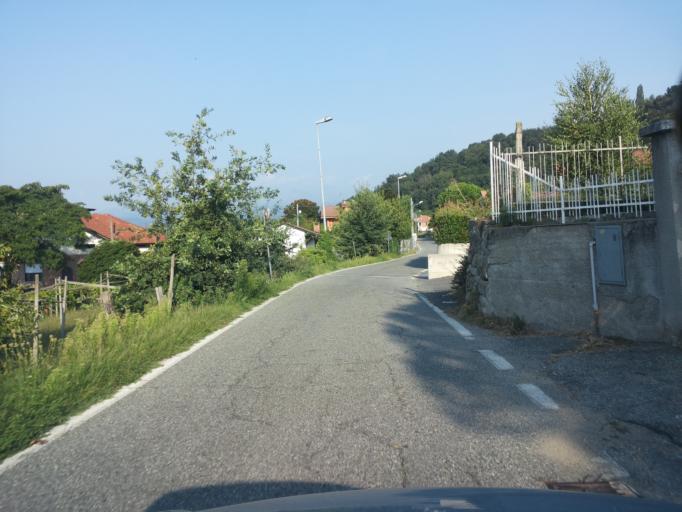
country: IT
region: Piedmont
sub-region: Provincia di Torino
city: Palazzo Canavese
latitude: 45.4607
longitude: 7.9817
